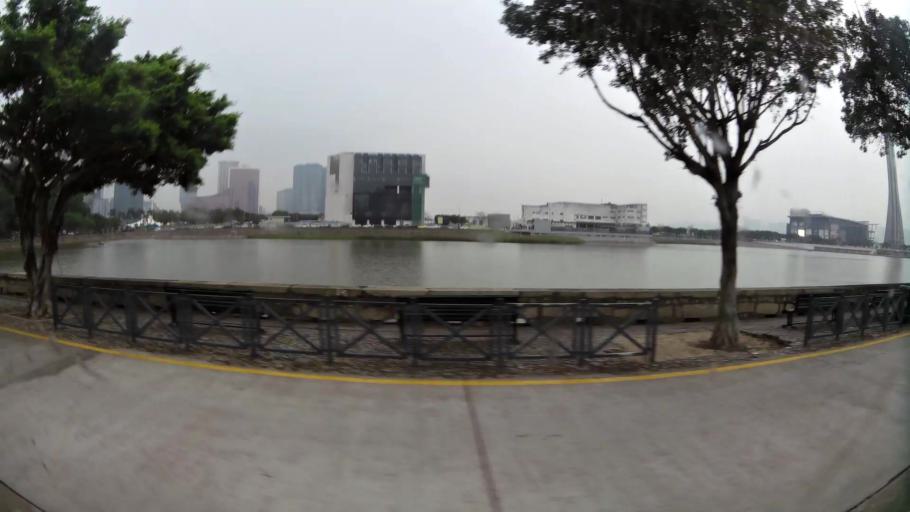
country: CN
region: Guangdong
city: Wanzai
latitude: 22.1848
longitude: 113.5350
